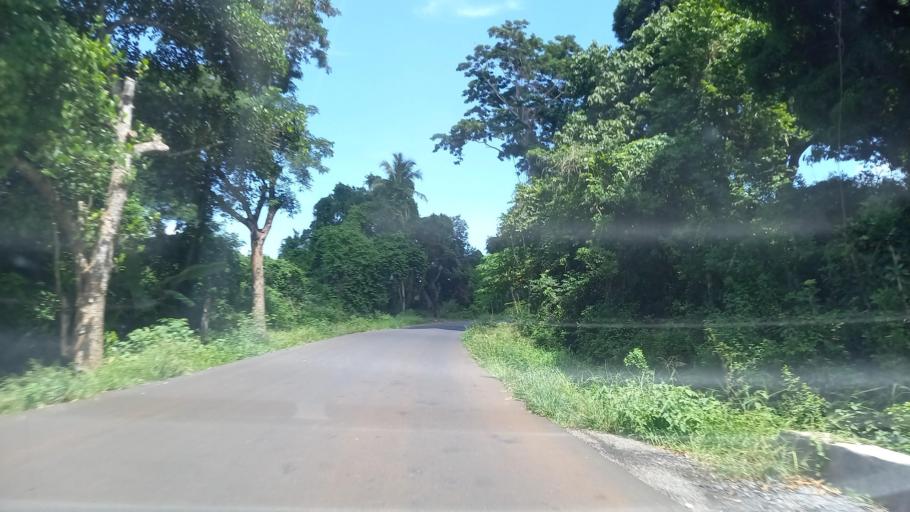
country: YT
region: M'Tsangamouji
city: M'Tsangamouji
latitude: -12.7545
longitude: 45.0655
